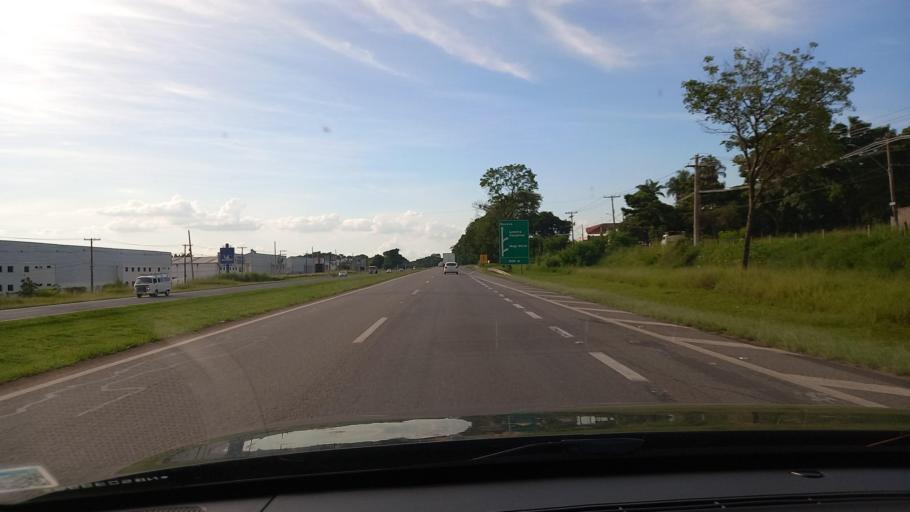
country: BR
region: Sao Paulo
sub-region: Mogi-Mirim
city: Mogi Mirim
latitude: -22.4469
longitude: -46.9834
